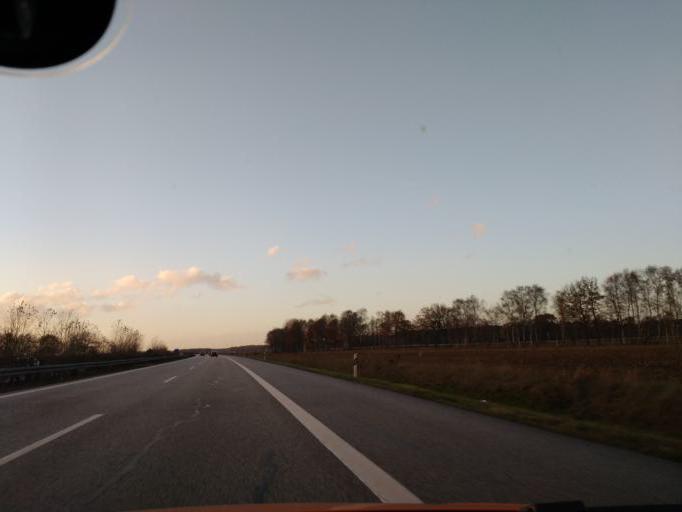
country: DE
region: Mecklenburg-Vorpommern
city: Sulstorf
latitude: 53.4655
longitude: 11.3372
